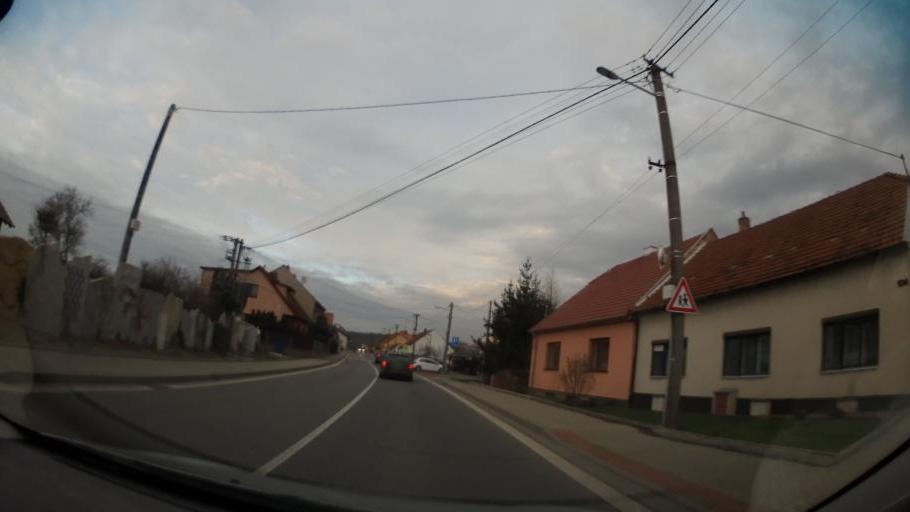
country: CZ
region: South Moravian
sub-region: Okres Brno-Venkov
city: Rosice
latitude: 49.1669
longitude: 16.4012
